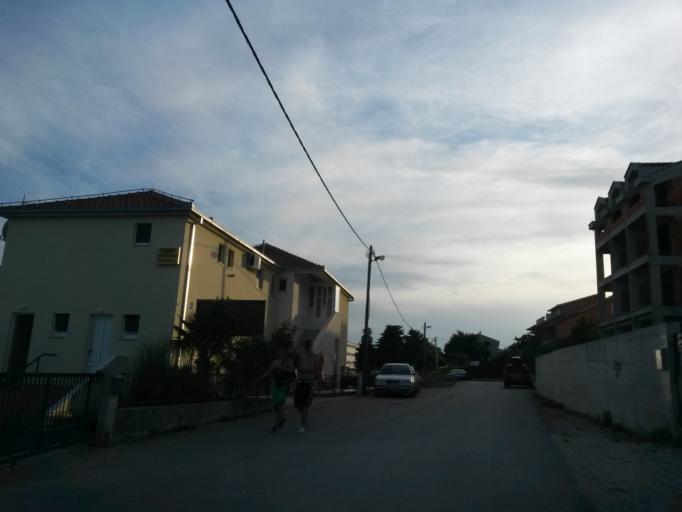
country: HR
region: Splitsko-Dalmatinska
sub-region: Grad Trogir
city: Trogir
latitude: 43.5428
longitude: 16.3186
